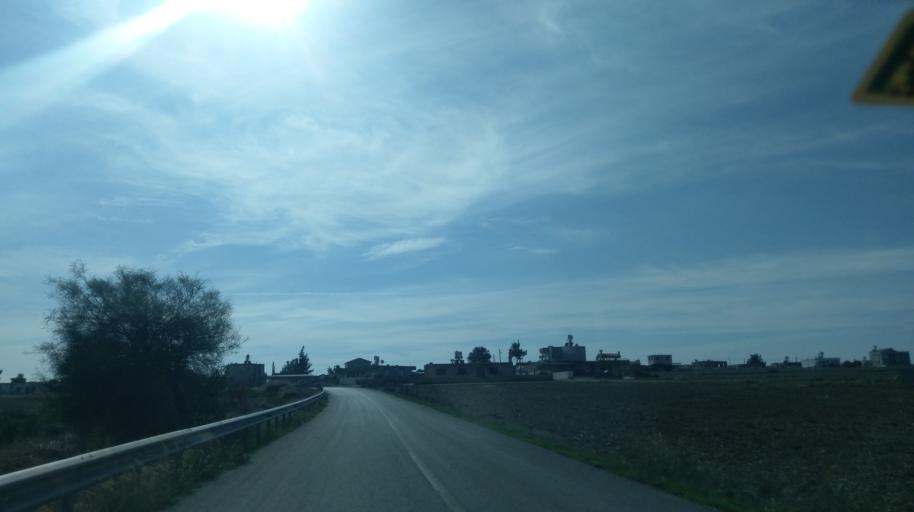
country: CY
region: Ammochostos
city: Lefkonoiko
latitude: 35.2220
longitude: 33.6971
